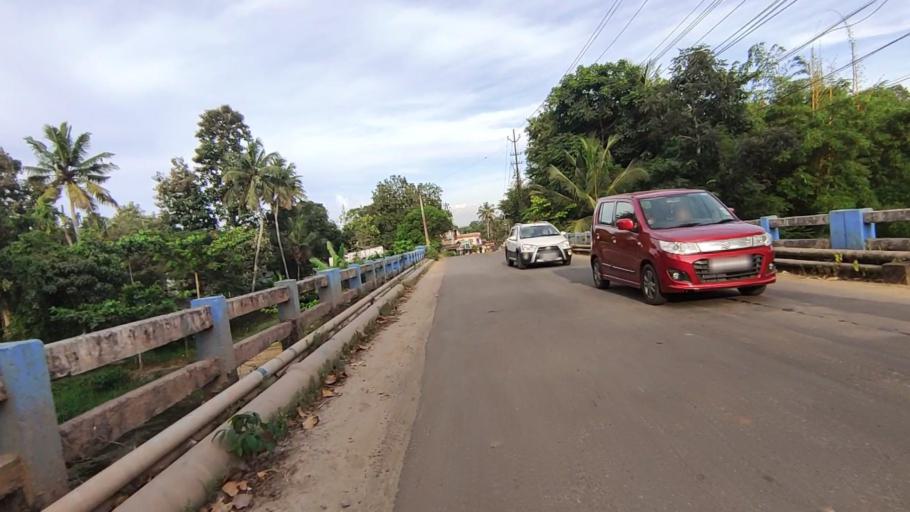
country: IN
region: Kerala
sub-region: Kottayam
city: Kottayam
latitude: 9.6104
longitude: 76.4937
